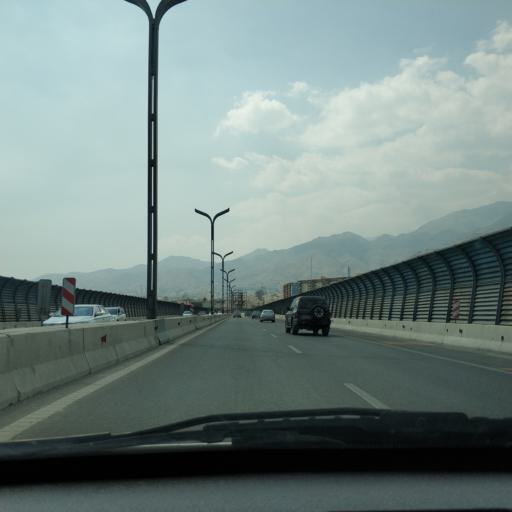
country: IR
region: Tehran
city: Tajrish
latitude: 35.7885
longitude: 51.4846
